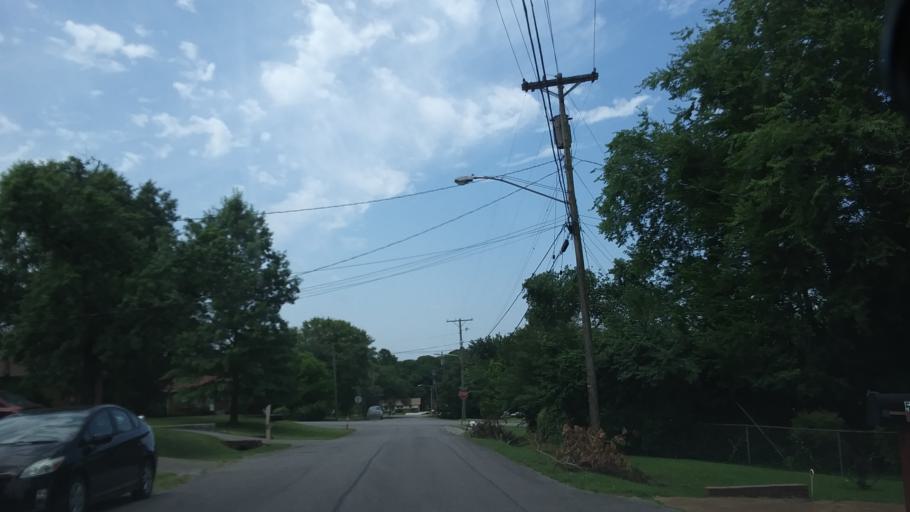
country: US
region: Tennessee
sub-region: Davidson County
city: Belle Meade
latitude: 36.1565
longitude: -86.8814
